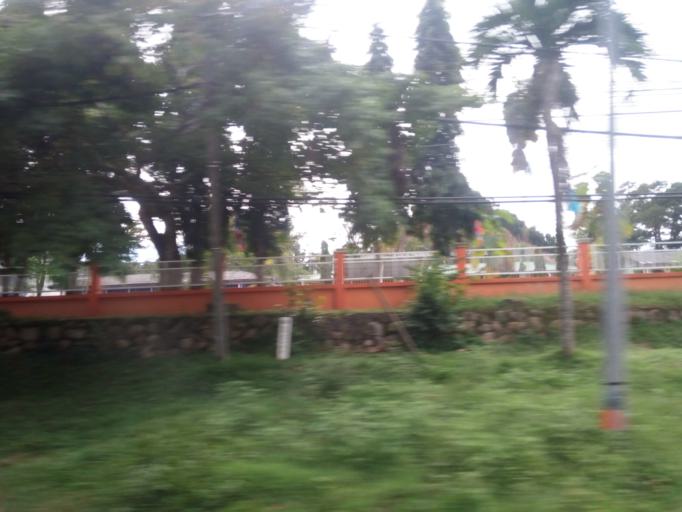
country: TH
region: Phuket
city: Mueang Phuket
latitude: 7.8409
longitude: 98.3900
